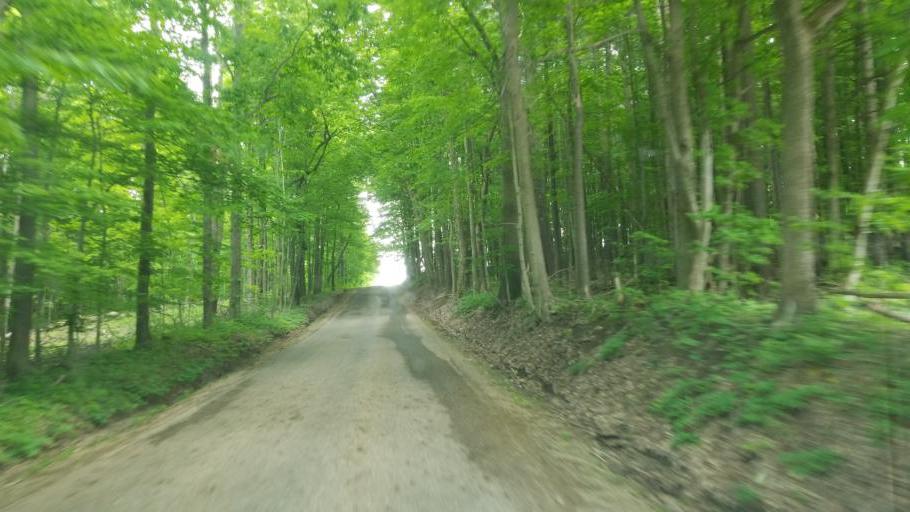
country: US
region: Ohio
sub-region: Sandusky County
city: Bellville
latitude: 40.6473
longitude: -82.4170
